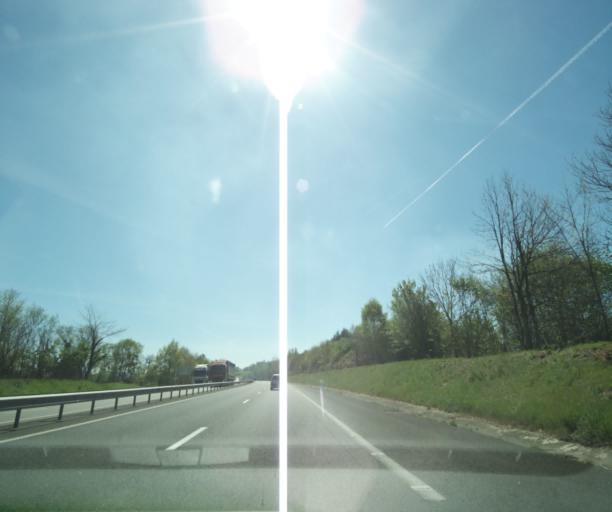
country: FR
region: Limousin
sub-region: Departement de la Correze
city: Uzerche
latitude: 45.4584
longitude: 1.5105
